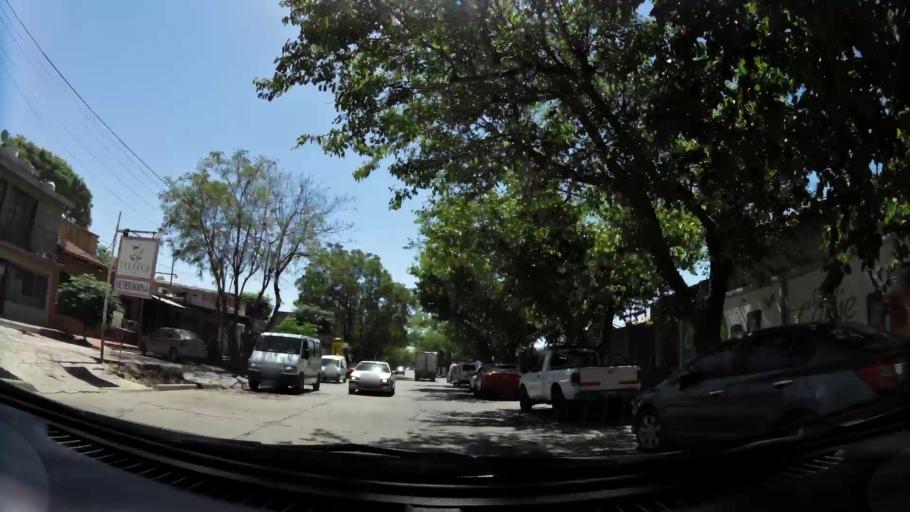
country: AR
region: Mendoza
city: Mendoza
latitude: -32.8827
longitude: -68.8133
